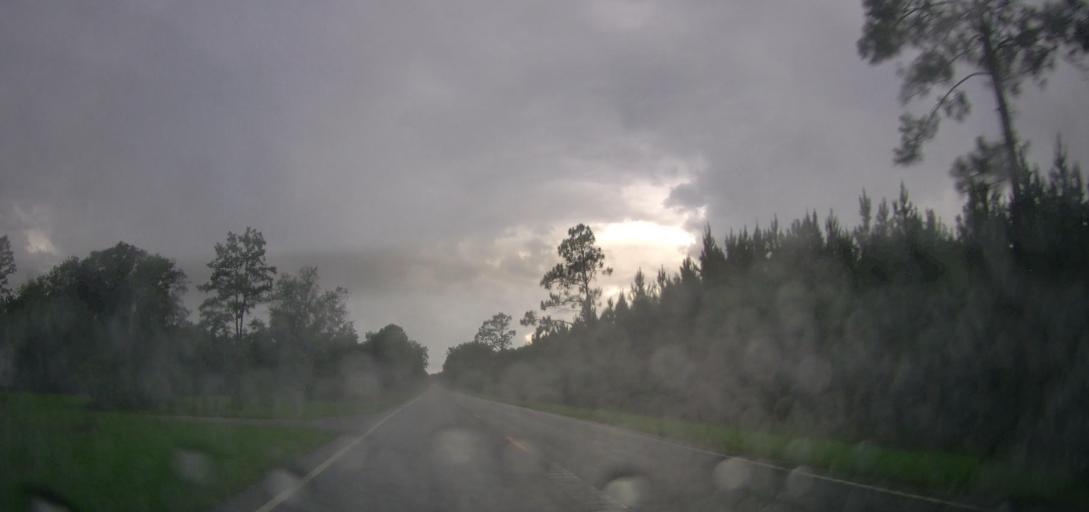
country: US
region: Georgia
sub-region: Brantley County
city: Nahunta
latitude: 31.3378
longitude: -81.7828
